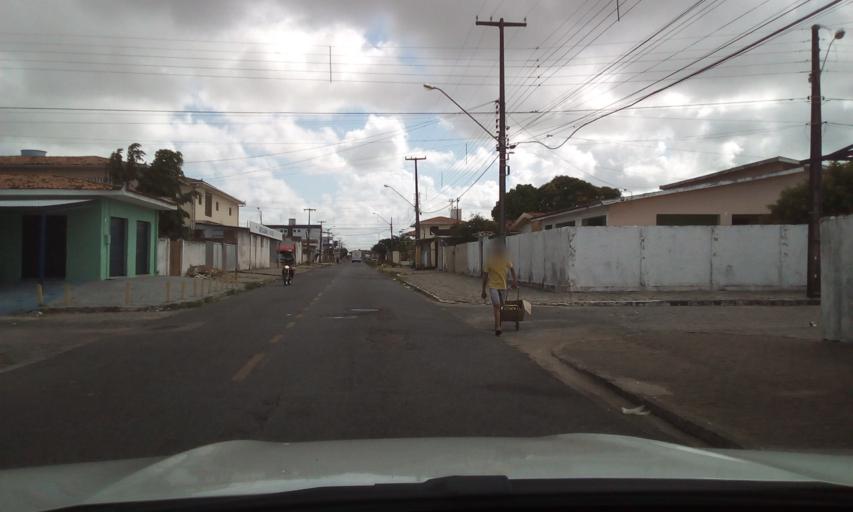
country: BR
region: Paraiba
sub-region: Joao Pessoa
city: Joao Pessoa
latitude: -7.1504
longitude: -34.8801
